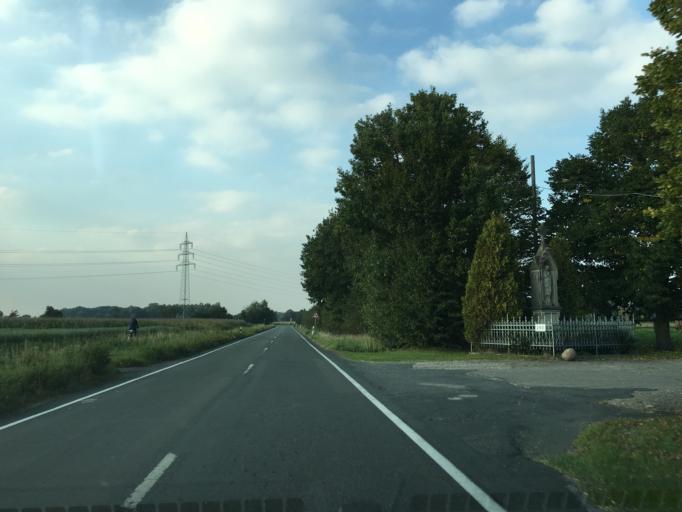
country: DE
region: North Rhine-Westphalia
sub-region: Regierungsbezirk Munster
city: Greven
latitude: 52.0358
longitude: 7.5534
